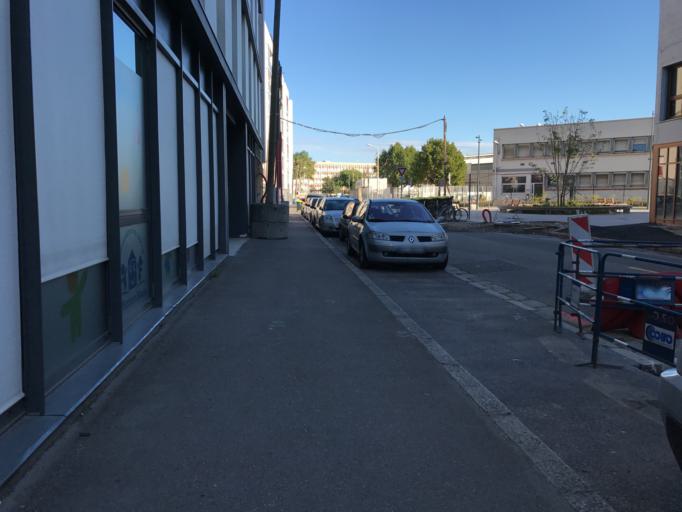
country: FR
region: Rhone-Alpes
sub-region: Departement du Rhone
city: Lyon
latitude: 45.7399
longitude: 4.8356
